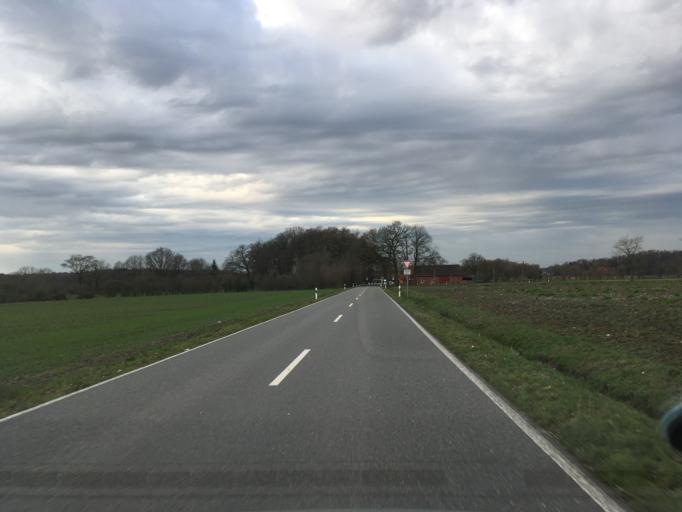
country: DE
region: North Rhine-Westphalia
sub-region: Regierungsbezirk Munster
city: Legden
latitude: 52.0549
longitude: 7.1647
